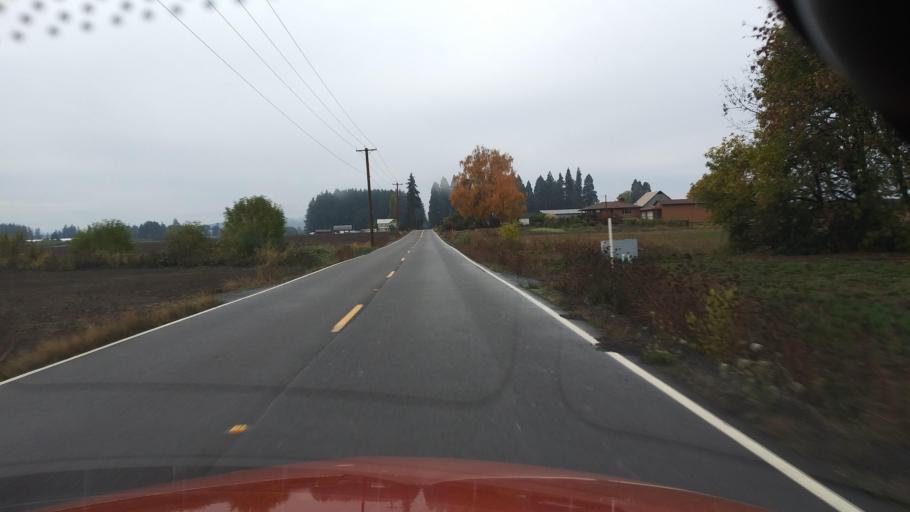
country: US
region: Oregon
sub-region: Washington County
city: Forest Grove
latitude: 45.5435
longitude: -123.0870
